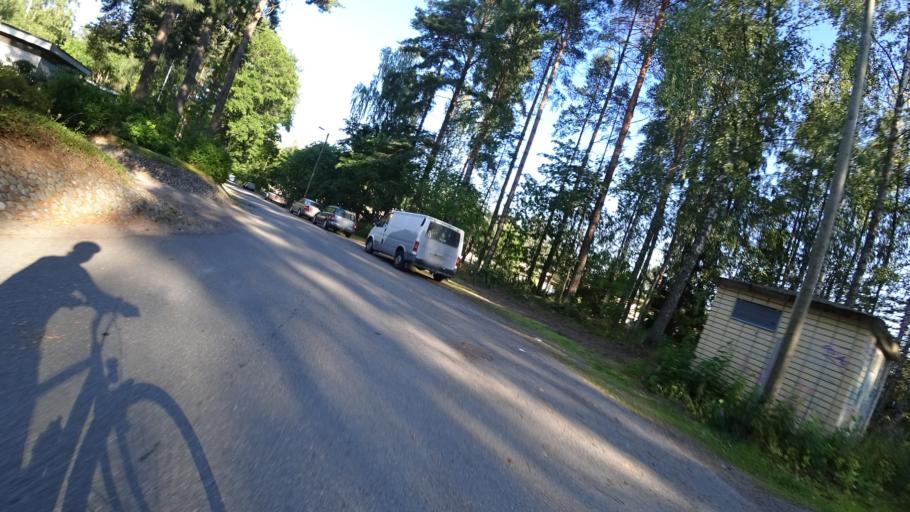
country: FI
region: Pirkanmaa
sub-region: Tampere
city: Pirkkala
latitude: 61.4949
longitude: 23.6111
